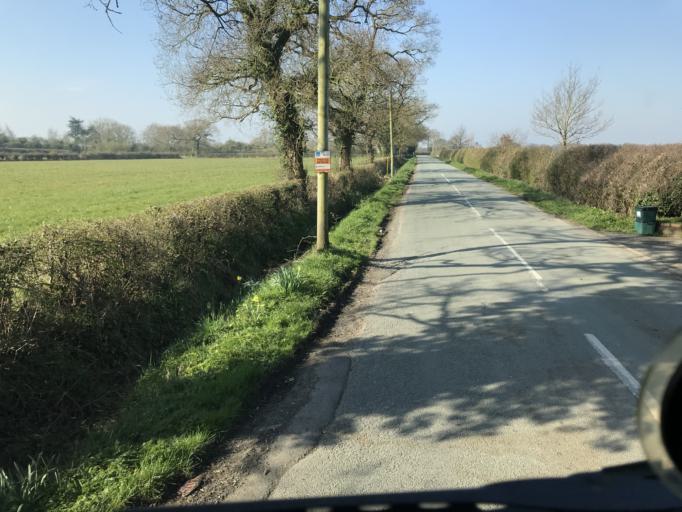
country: GB
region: England
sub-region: Cheshire West and Chester
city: Waverton
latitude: 53.1406
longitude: -2.8110
